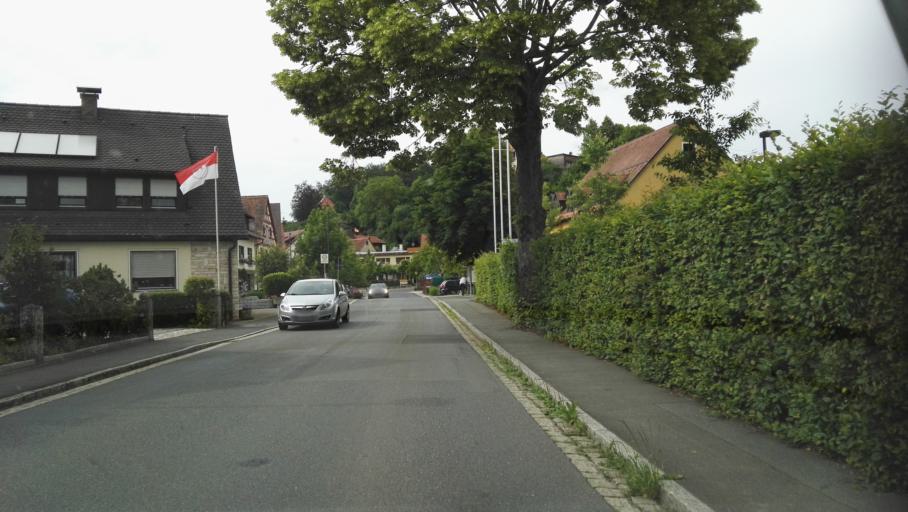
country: DE
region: Bavaria
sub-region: Upper Franconia
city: Waischenfeld
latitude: 49.8435
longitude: 11.3483
